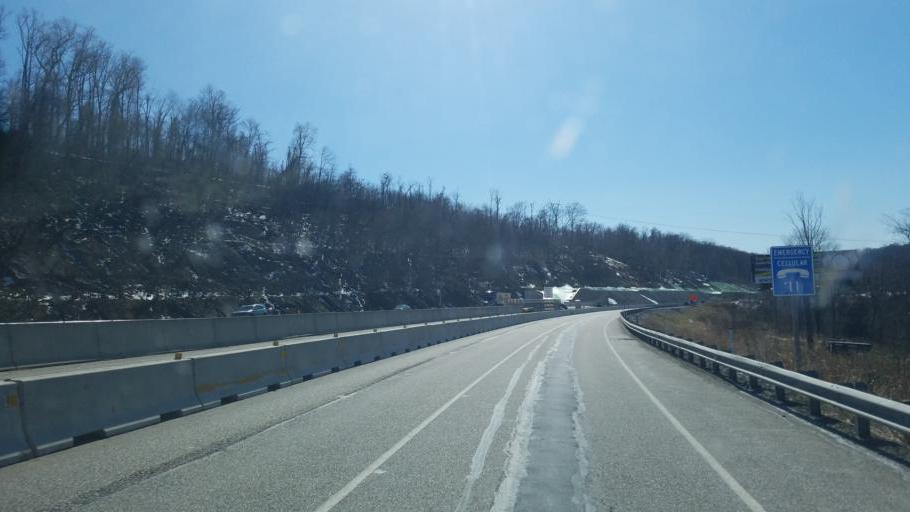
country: US
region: Pennsylvania
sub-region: Dauphin County
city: Highspire
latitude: 40.1985
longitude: -76.8116
